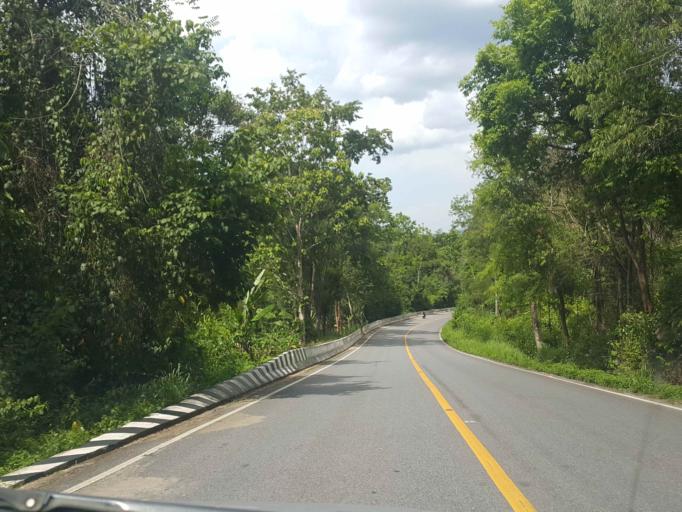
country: TH
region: Nan
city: Nan
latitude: 18.8666
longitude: 100.6261
